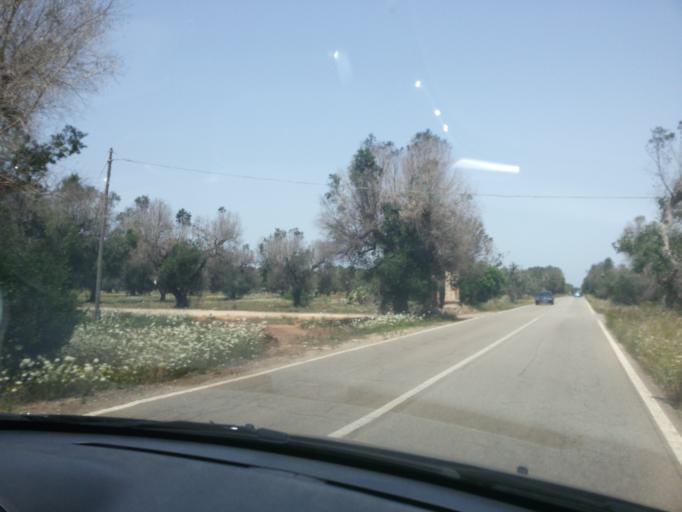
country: IT
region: Apulia
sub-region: Provincia di Lecce
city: Veglie
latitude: 40.3139
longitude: 17.9215
